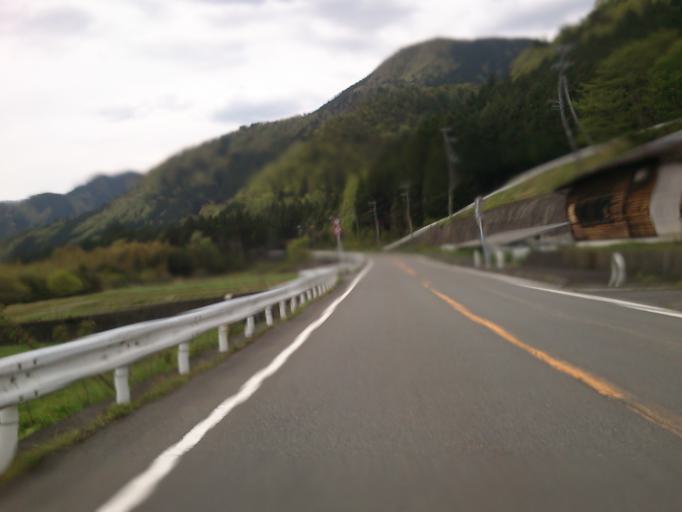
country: JP
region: Kyoto
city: Maizuru
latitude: 35.2800
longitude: 135.5396
